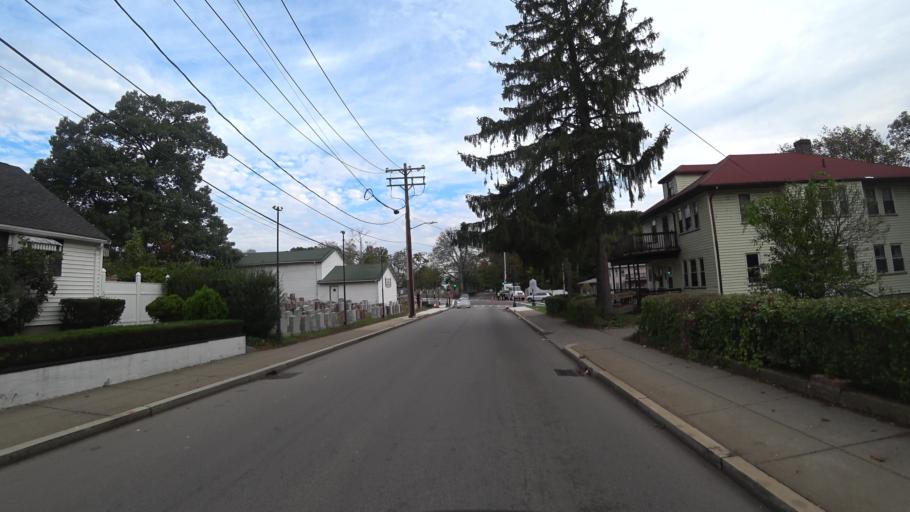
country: US
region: Massachusetts
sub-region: Suffolk County
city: Jamaica Plain
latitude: 42.2737
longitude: -71.1095
